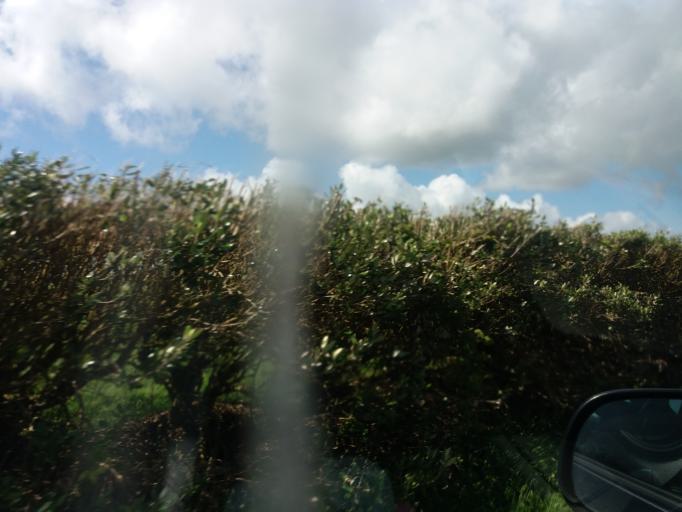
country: IE
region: Munster
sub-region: Waterford
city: Dunmore East
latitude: 52.1632
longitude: -6.8938
